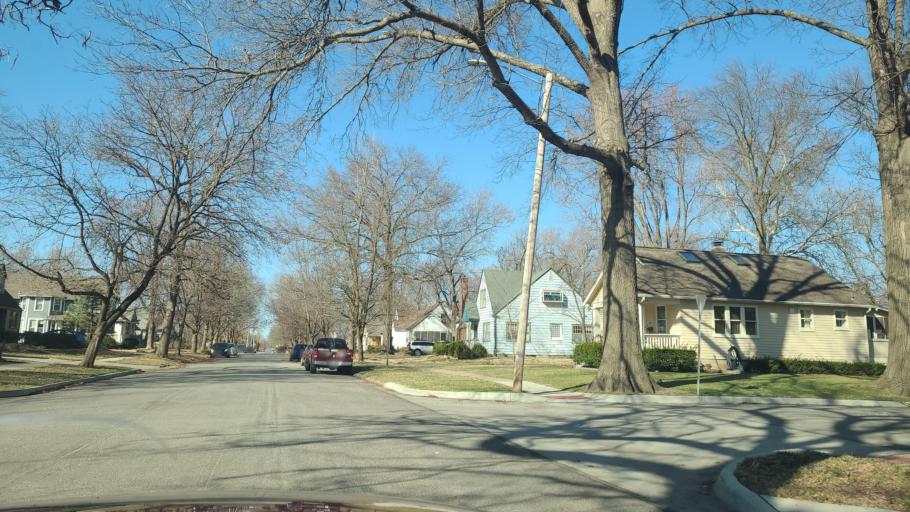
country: US
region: Kansas
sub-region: Douglas County
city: Lawrence
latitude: 38.9481
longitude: -95.2347
